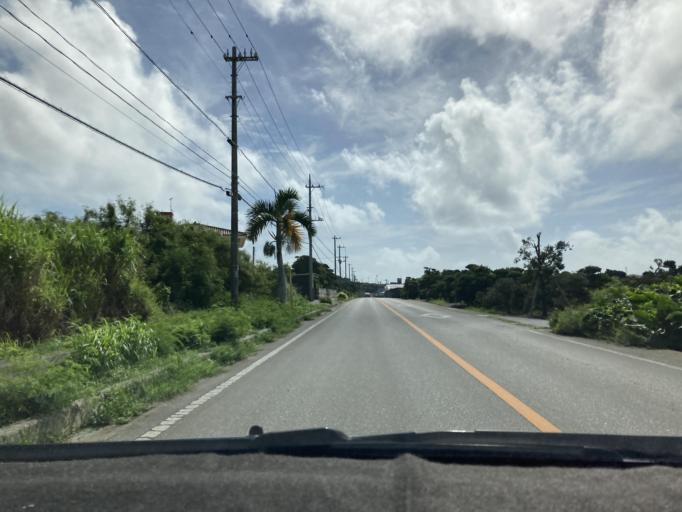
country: JP
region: Okinawa
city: Itoman
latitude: 26.1006
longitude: 127.6737
